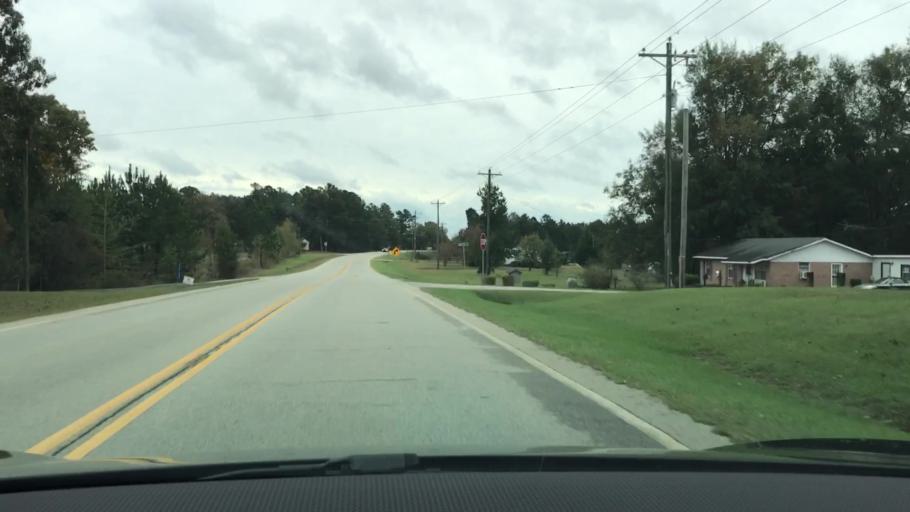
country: US
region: Georgia
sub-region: Jefferson County
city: Wrens
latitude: 33.1900
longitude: -82.4574
